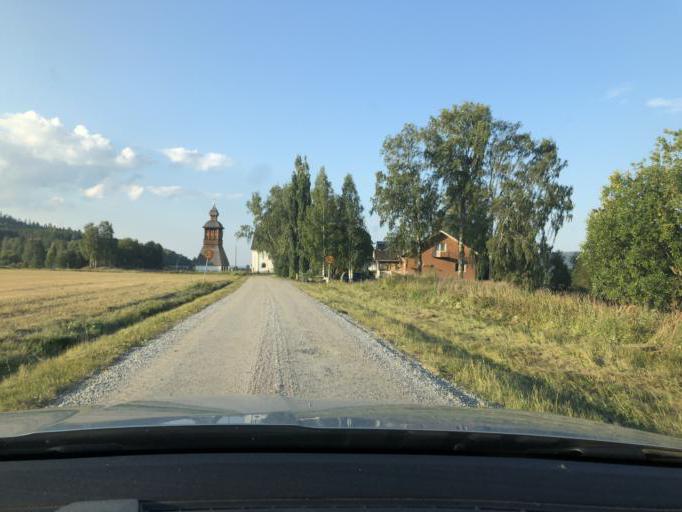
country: SE
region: Vaesternorrland
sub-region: Kramfors Kommun
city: Bollstabruk
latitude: 63.0780
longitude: 17.7408
